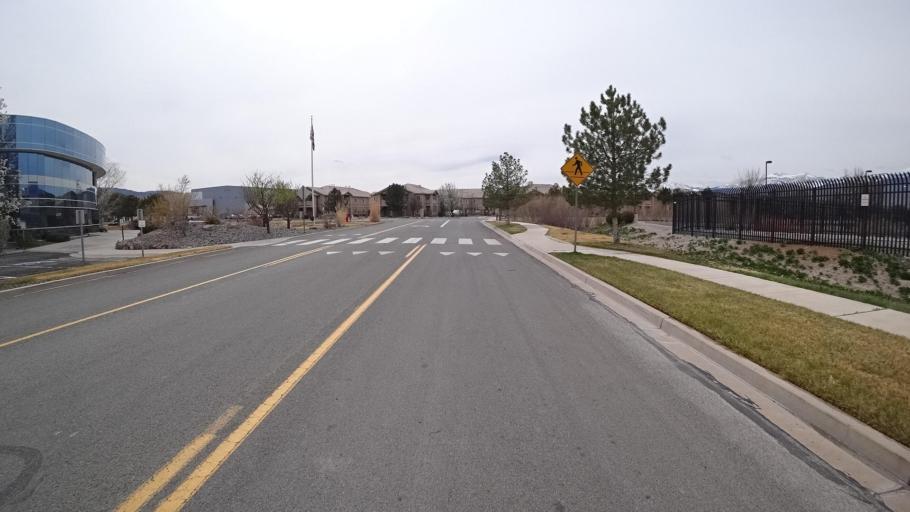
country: US
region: Nevada
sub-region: Washoe County
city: Sparks
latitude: 39.4522
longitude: -119.7542
